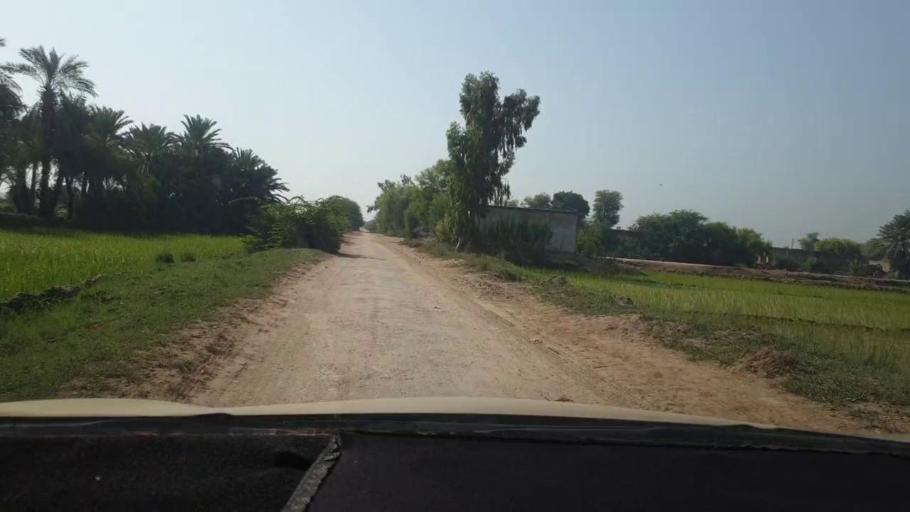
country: PK
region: Sindh
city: Miro Khan
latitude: 27.7262
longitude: 68.1201
